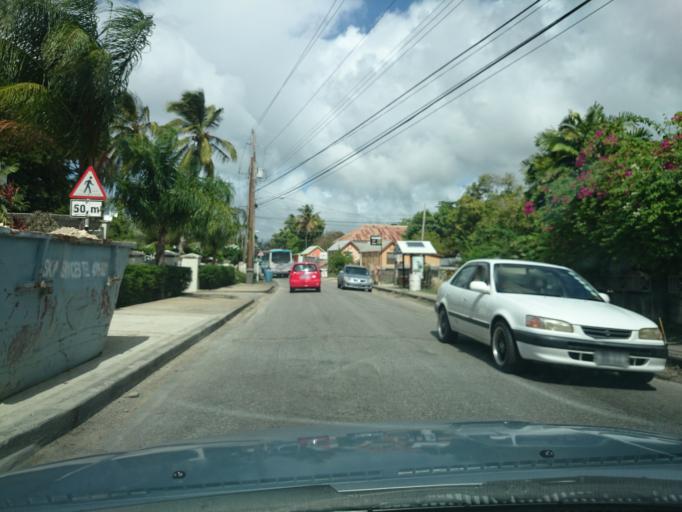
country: BB
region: Saint James
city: Holetown
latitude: 13.1495
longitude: -59.6380
